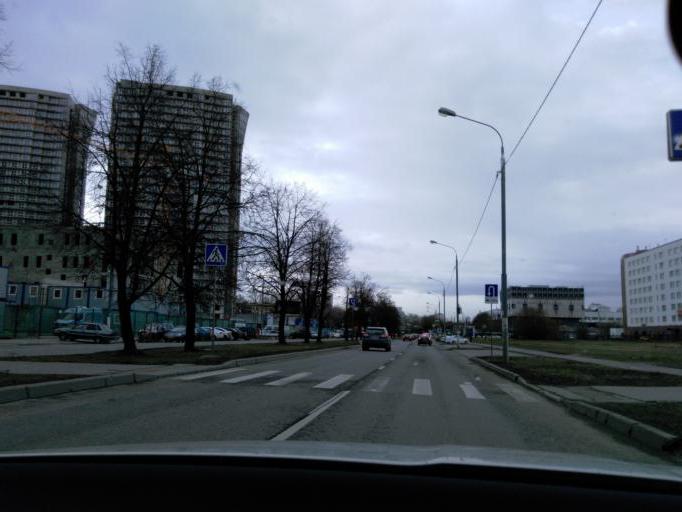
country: RU
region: Moscow
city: Golovinskiy
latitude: 55.8545
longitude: 37.4943
